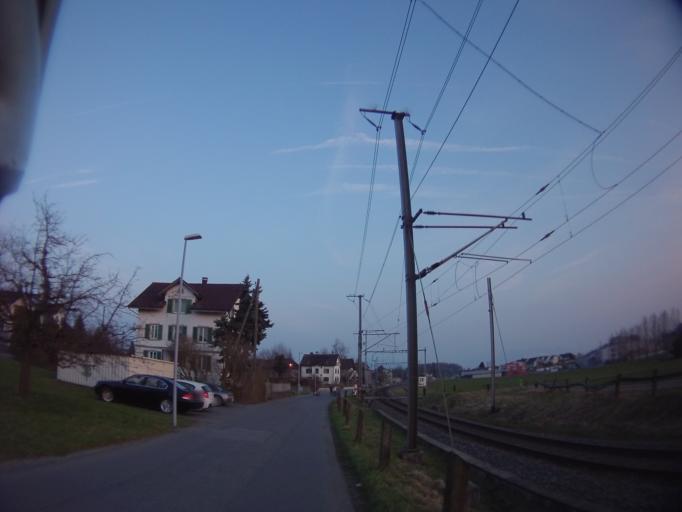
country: CH
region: Zurich
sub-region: Bezirk Affoltern
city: Mettmenstetten
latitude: 47.2482
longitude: 8.4551
